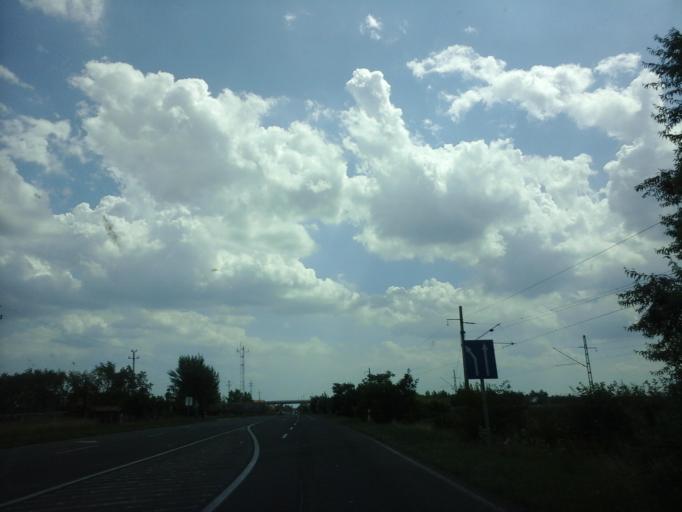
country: HU
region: Gyor-Moson-Sopron
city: Rajka
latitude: 48.0075
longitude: 17.1839
